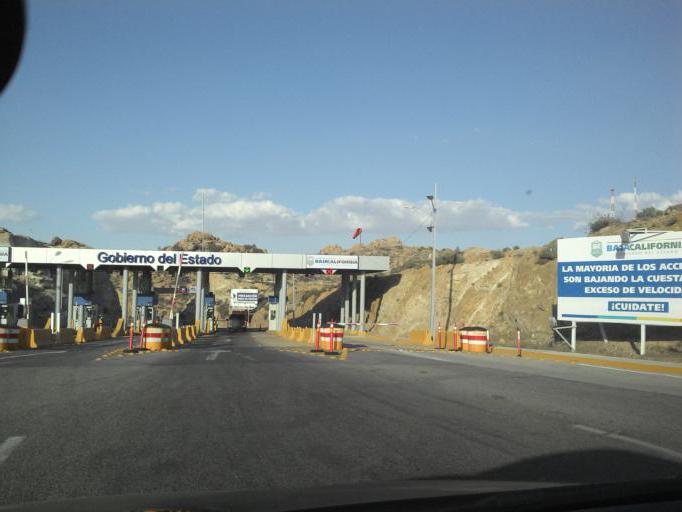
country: MX
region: Baja California
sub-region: Tecate
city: Cereso del Hongo
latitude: 32.5557
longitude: -116.0371
